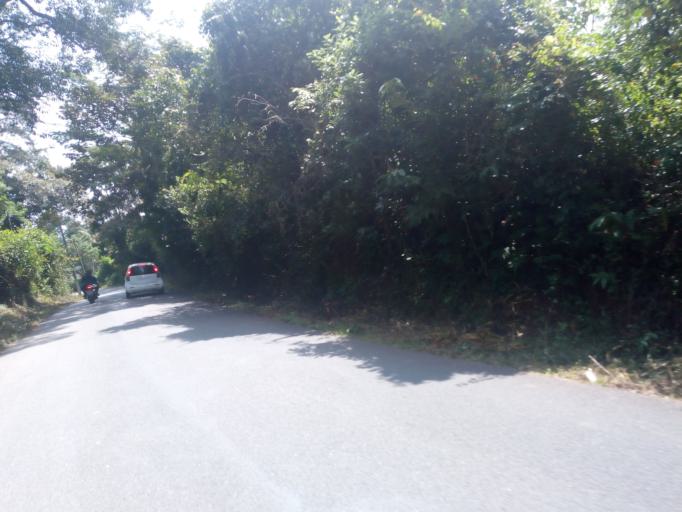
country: IN
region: Karnataka
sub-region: Kodagu
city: Ponnampet
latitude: 12.0626
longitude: 75.9534
